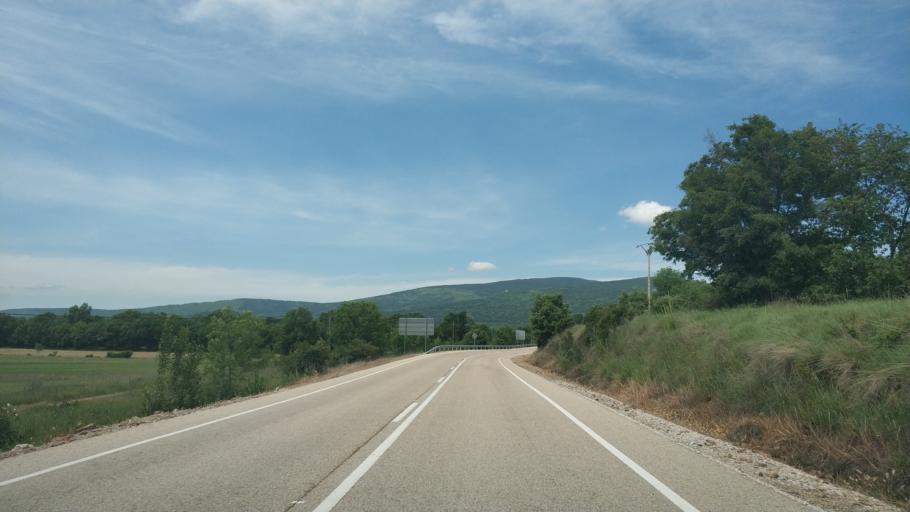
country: ES
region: Castille and Leon
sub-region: Provincia de Soria
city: Sotillo del Rincon
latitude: 41.8919
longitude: -2.6332
